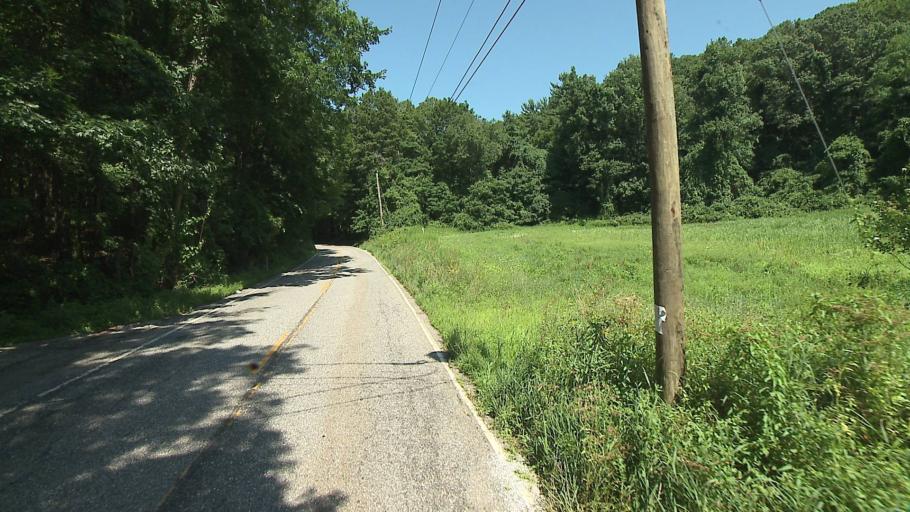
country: US
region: New York
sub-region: Dutchess County
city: Pine Plains
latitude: 41.9210
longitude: -73.4939
